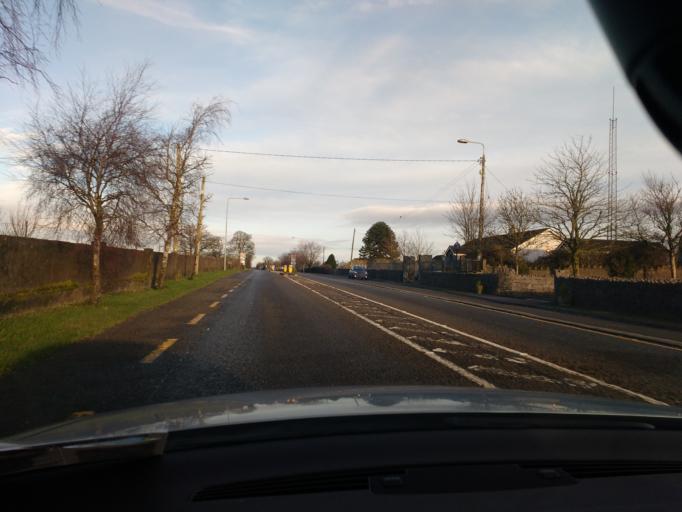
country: IE
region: Munster
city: Thurles
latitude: 52.6405
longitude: -7.7359
